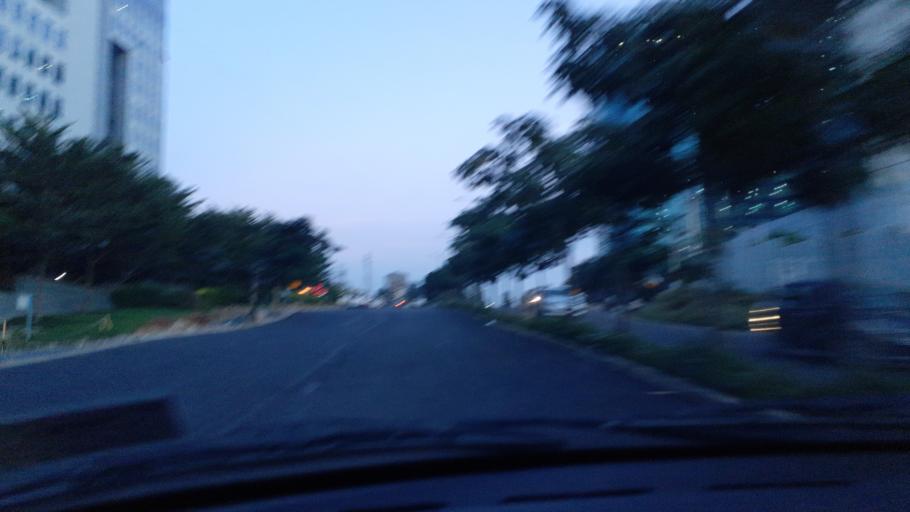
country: IN
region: Telangana
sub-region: Rangareddi
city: Kukatpalli
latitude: 17.4432
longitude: 78.3687
